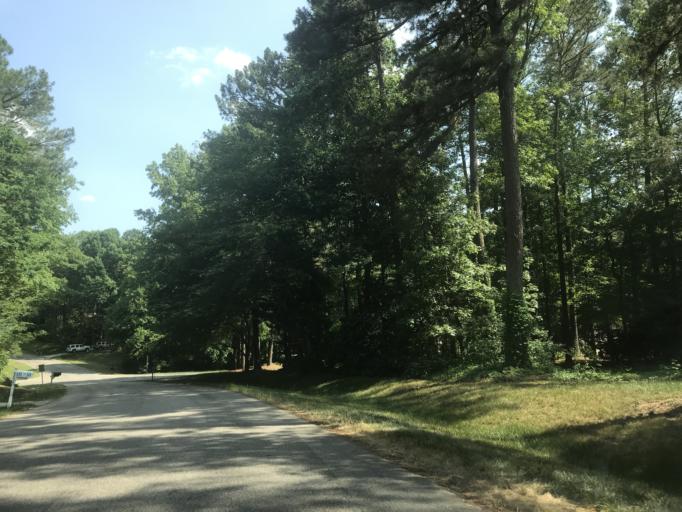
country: US
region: North Carolina
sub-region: Wake County
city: West Raleigh
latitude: 35.8994
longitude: -78.6876
